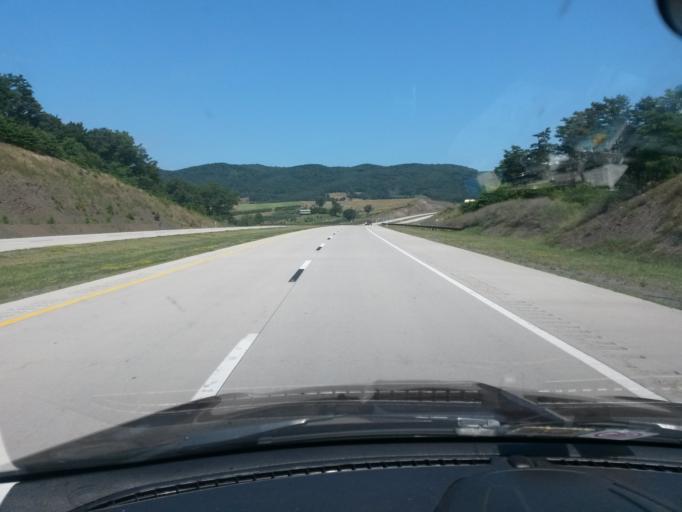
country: US
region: West Virginia
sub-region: Grant County
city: Petersburg
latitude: 39.1403
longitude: -79.1199
